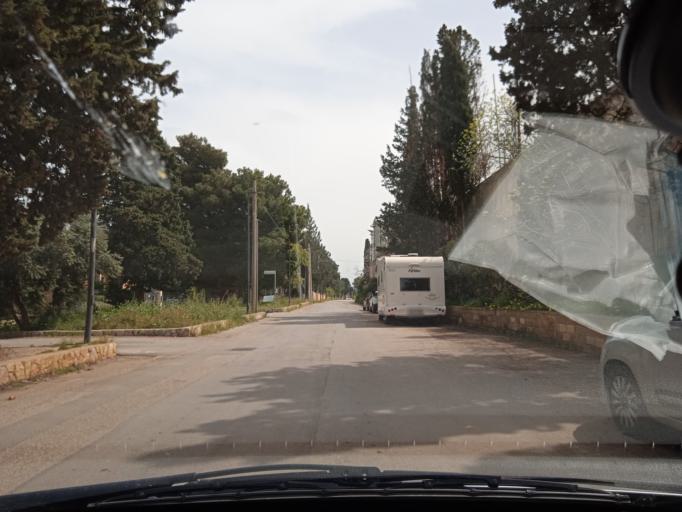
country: IT
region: Sicily
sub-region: Palermo
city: Torre Colonna-Sperone
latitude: 38.0239
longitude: 13.5775
